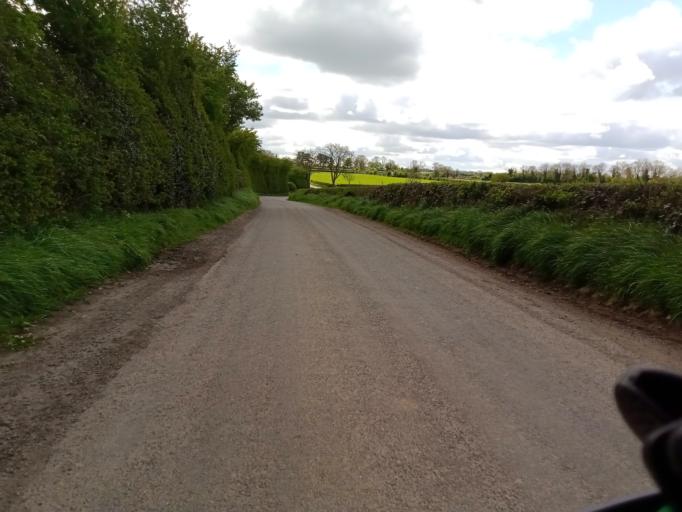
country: IE
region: Leinster
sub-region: Kilkenny
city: Thomastown
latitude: 52.5952
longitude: -7.1514
